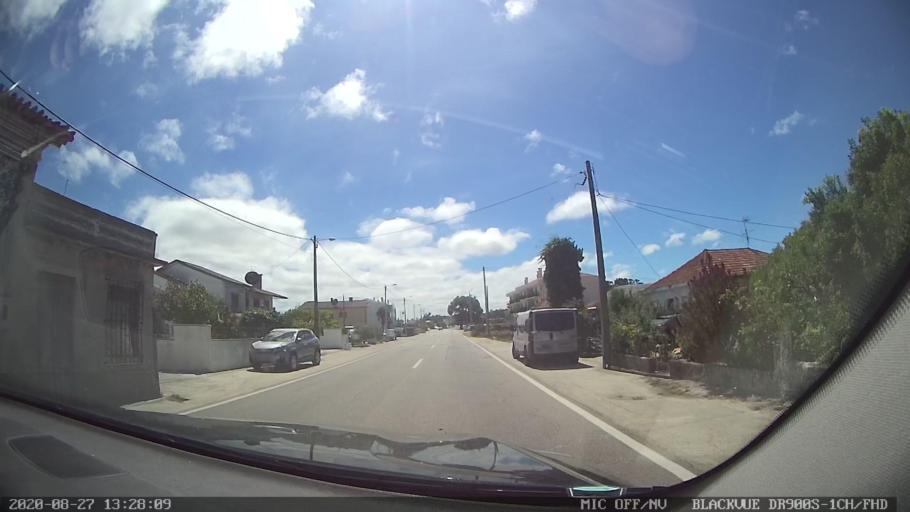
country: PT
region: Aveiro
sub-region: Vagos
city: Vagos
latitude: 40.5234
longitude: -8.6793
